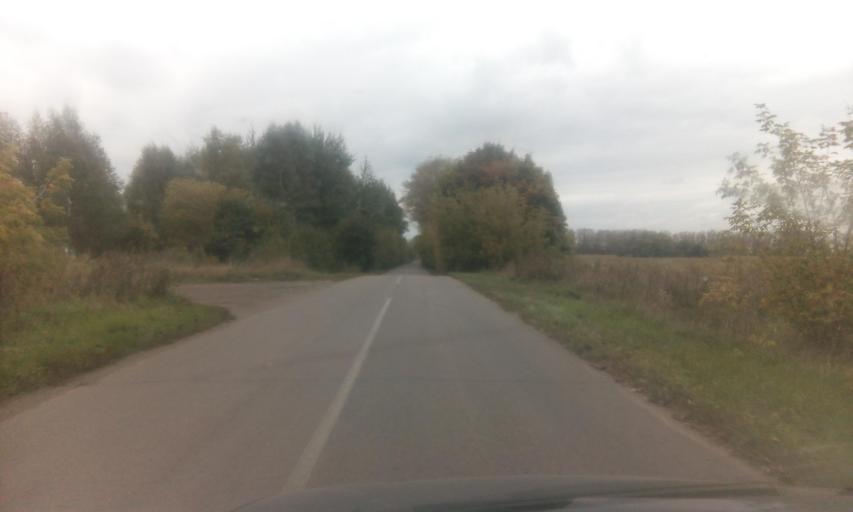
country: RU
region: Tula
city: Dubovka
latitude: 53.9569
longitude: 38.0608
